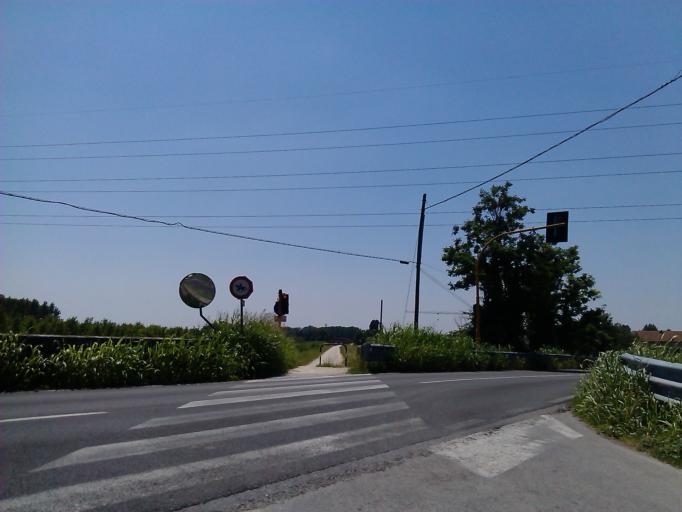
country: IT
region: Veneto
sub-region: Provincia di Padova
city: Camposampiero
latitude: 45.5801
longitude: 11.9392
